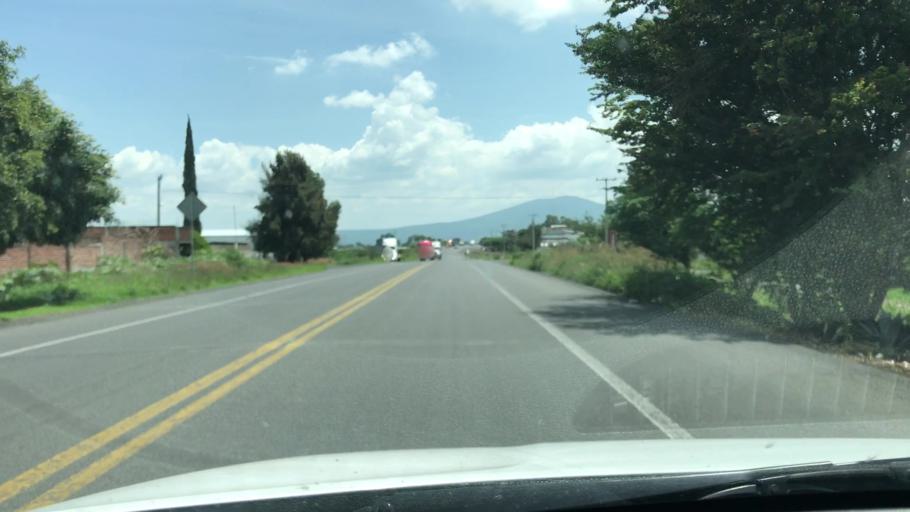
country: MX
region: Michoacan
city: Tanhuato de Guerrero
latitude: 20.2890
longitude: -102.3378
